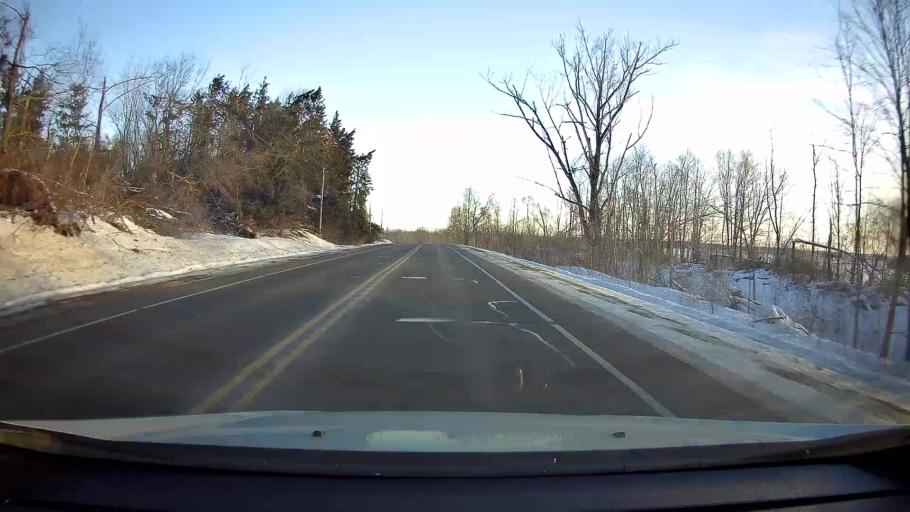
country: US
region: Wisconsin
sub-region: Barron County
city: Cumberland
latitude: 45.4691
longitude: -92.0868
